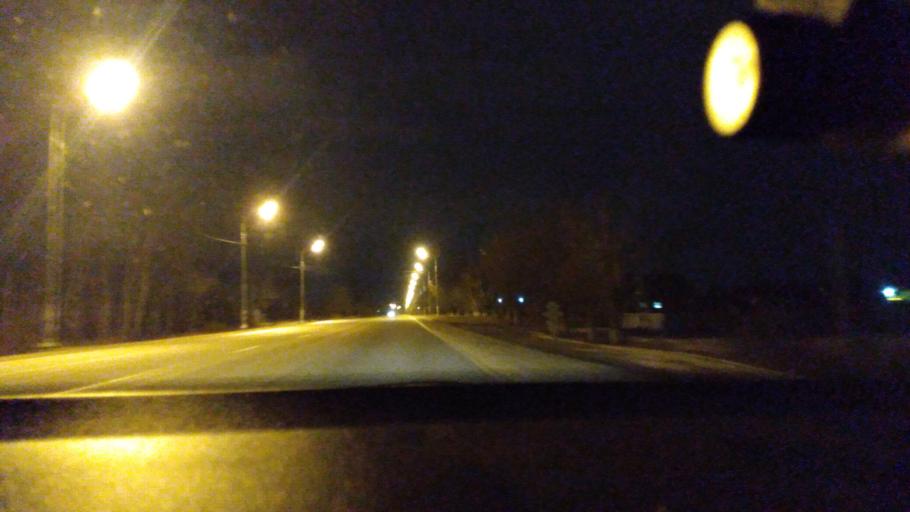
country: RU
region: Moskovskaya
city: Raduzhnyy
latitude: 55.1944
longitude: 38.6229
